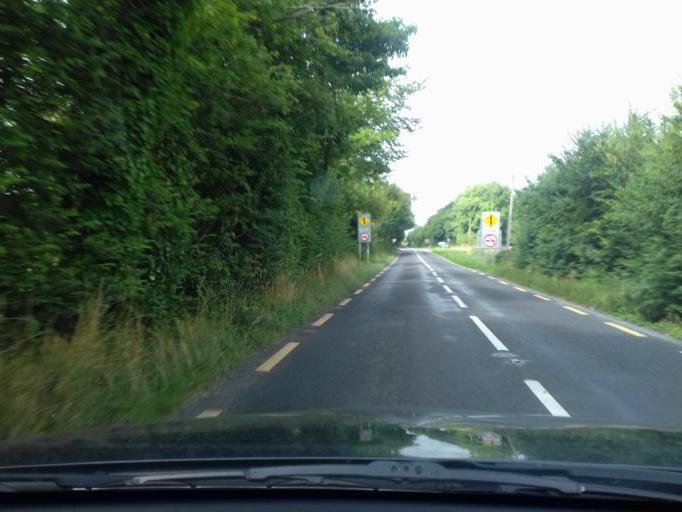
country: IE
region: Leinster
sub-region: County Carlow
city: Tullow
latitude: 52.8409
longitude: -6.7194
